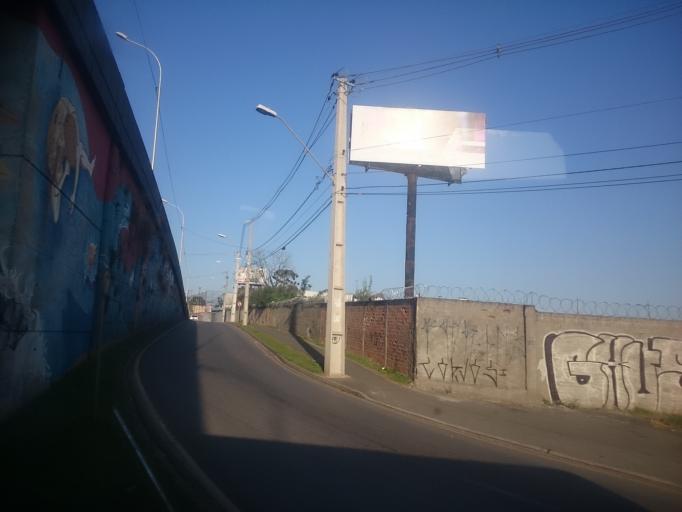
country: BR
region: Parana
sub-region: Curitiba
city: Curitiba
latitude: -25.4961
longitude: -49.2754
